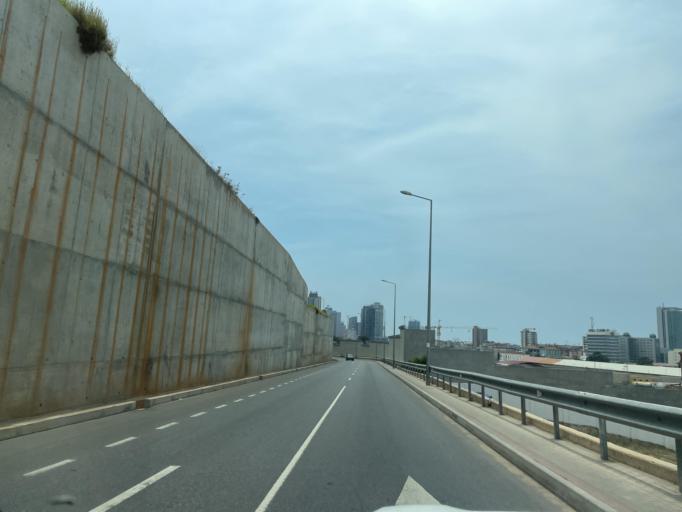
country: AO
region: Luanda
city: Luanda
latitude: -8.8048
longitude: 13.2500
